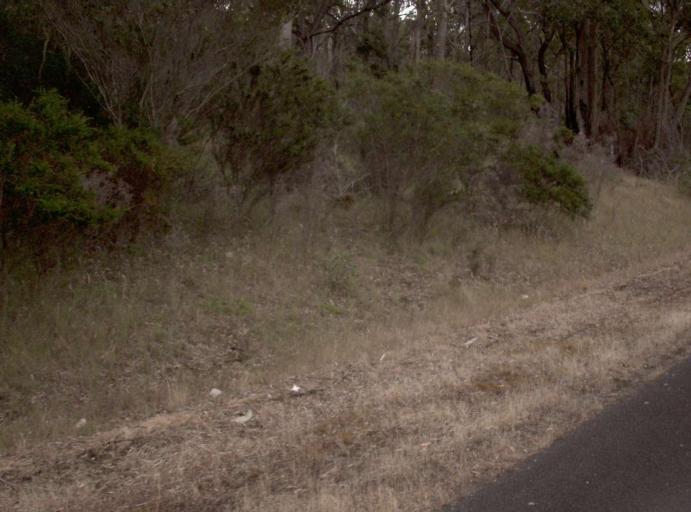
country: AU
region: Victoria
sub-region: Wellington
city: Sale
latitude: -38.4542
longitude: 146.9386
